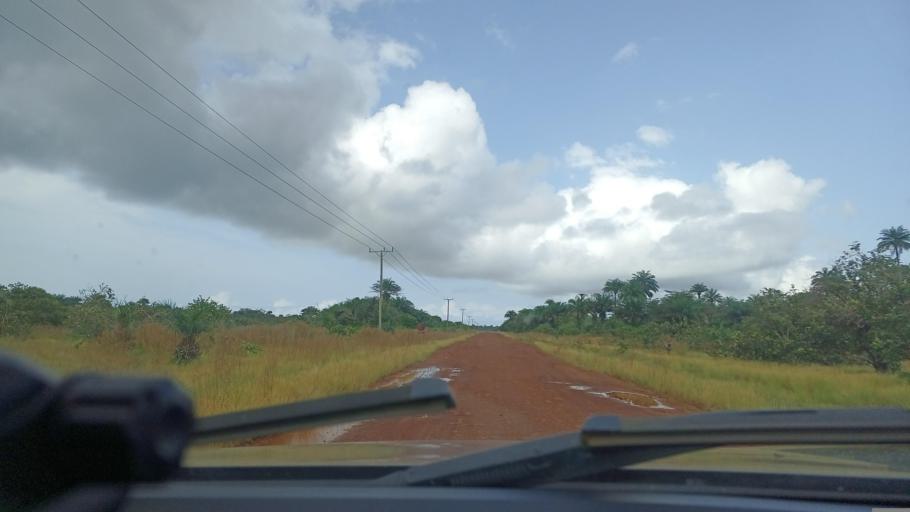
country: LR
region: Grand Cape Mount
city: Robertsport
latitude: 6.6914
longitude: -11.2690
